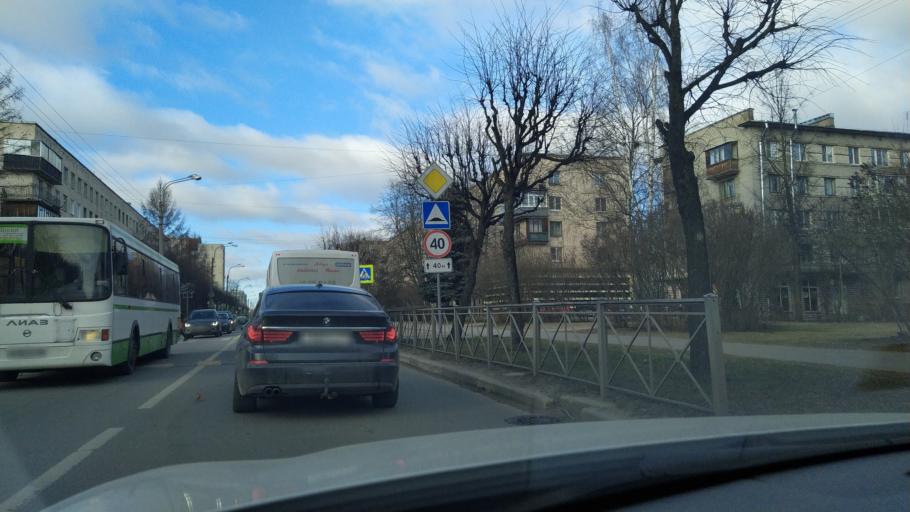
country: RU
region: St.-Petersburg
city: Pushkin
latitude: 59.7290
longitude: 30.4105
